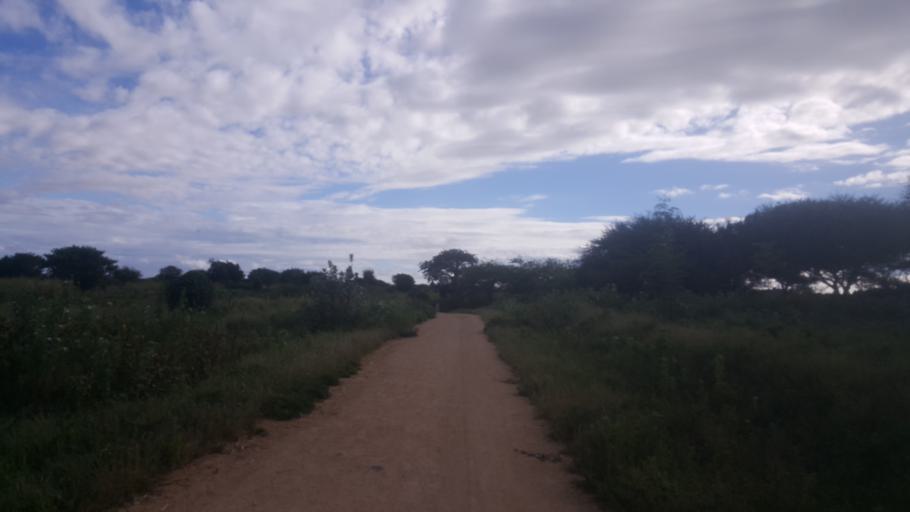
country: TZ
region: Dodoma
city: Dodoma
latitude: -6.0910
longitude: 35.5288
